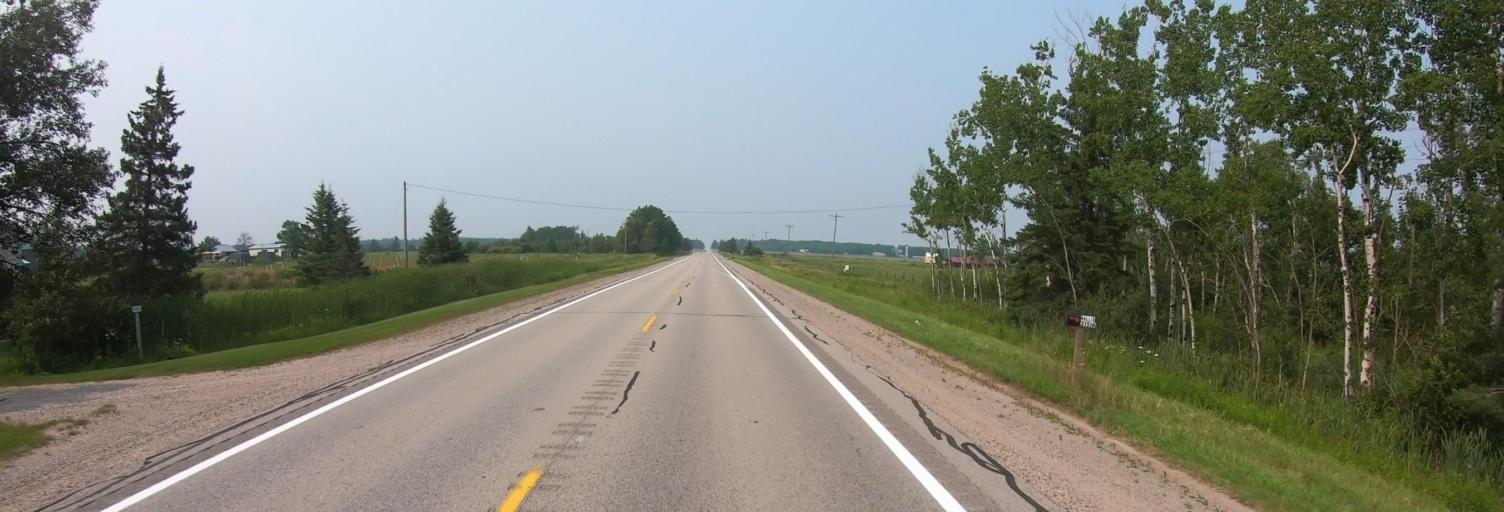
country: US
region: Michigan
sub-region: Chippewa County
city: Sault Ste. Marie
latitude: 46.1936
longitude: -84.3635
